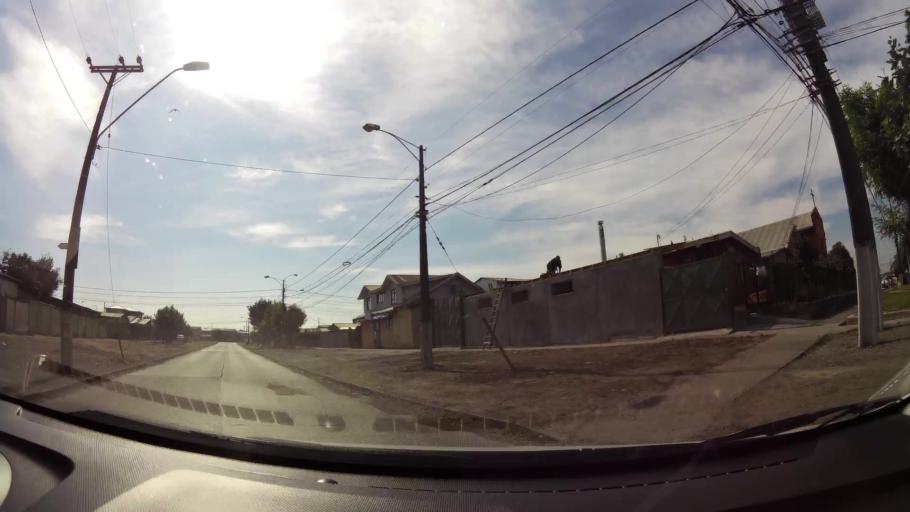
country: CL
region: Biobio
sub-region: Provincia de Concepcion
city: Talcahuano
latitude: -36.7891
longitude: -73.1114
